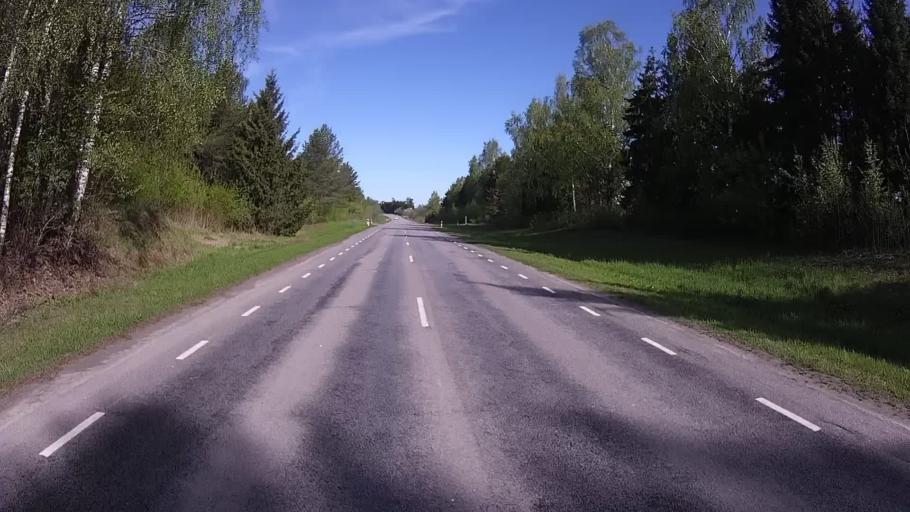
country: EE
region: Polvamaa
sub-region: Polva linn
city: Polva
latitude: 58.2374
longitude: 27.0163
